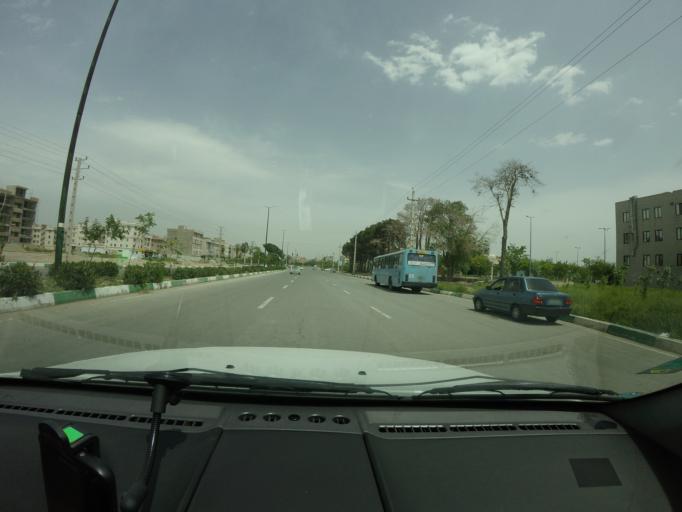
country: IR
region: Tehran
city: Eslamshahr
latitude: 35.5295
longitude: 51.2118
